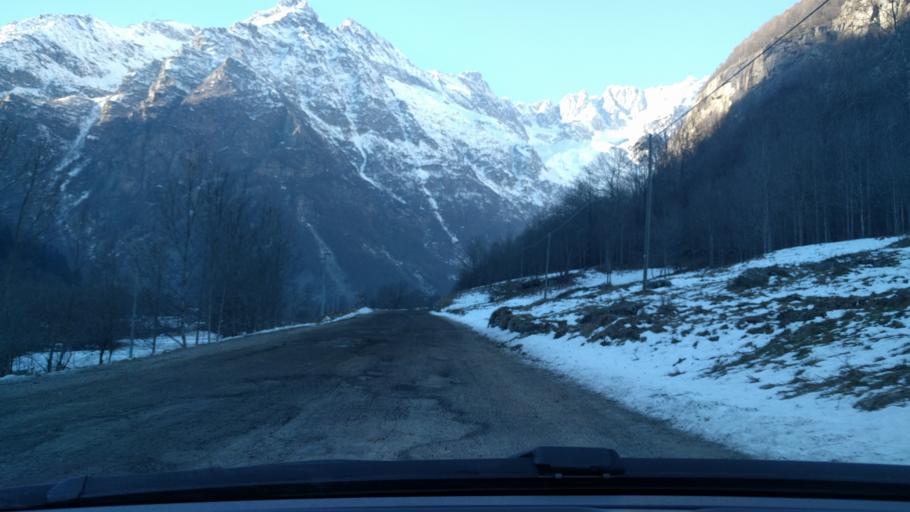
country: IT
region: Piedmont
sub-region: Provincia di Torino
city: Groscavallo
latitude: 45.3659
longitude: 7.2364
